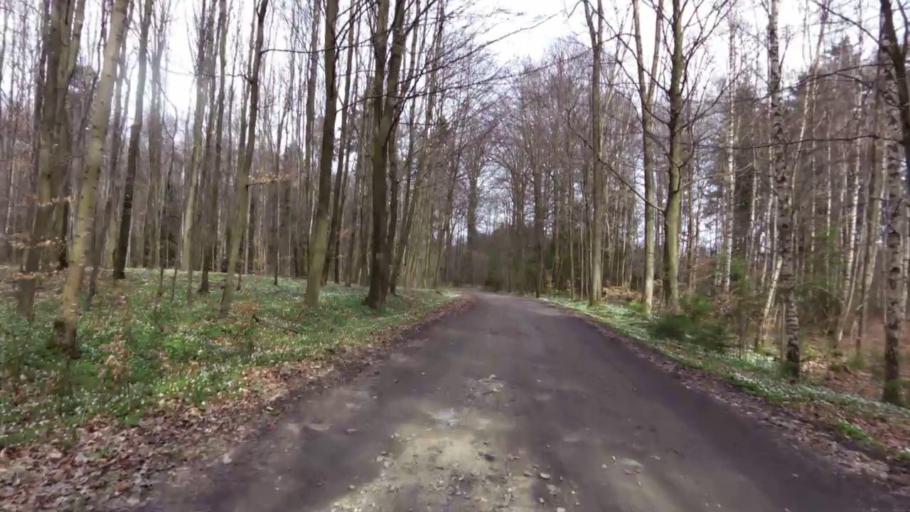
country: PL
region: West Pomeranian Voivodeship
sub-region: Powiat koszalinski
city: Sianow
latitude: 54.2682
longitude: 16.3194
